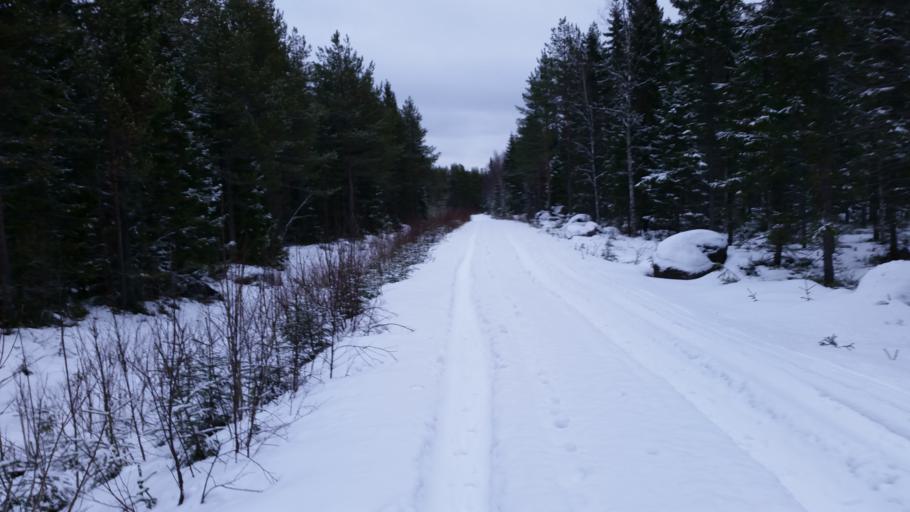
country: SE
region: Vaesterbotten
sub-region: Umea Kommun
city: Saevar
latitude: 63.9177
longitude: 20.7759
